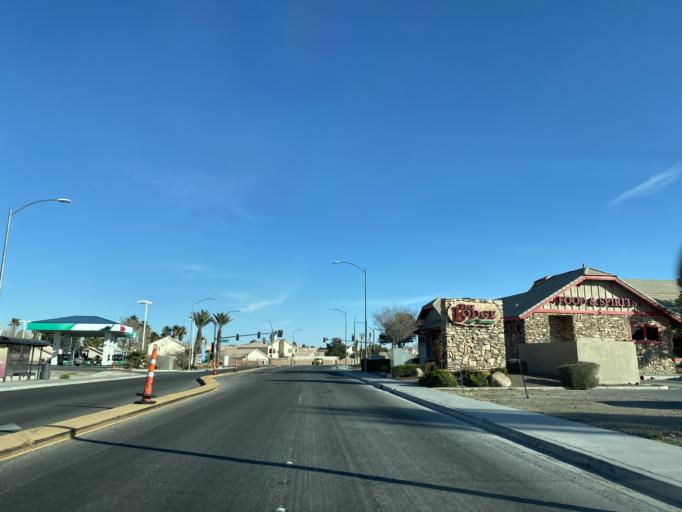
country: US
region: Nevada
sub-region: Clark County
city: Las Vegas
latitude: 36.2647
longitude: -115.2530
